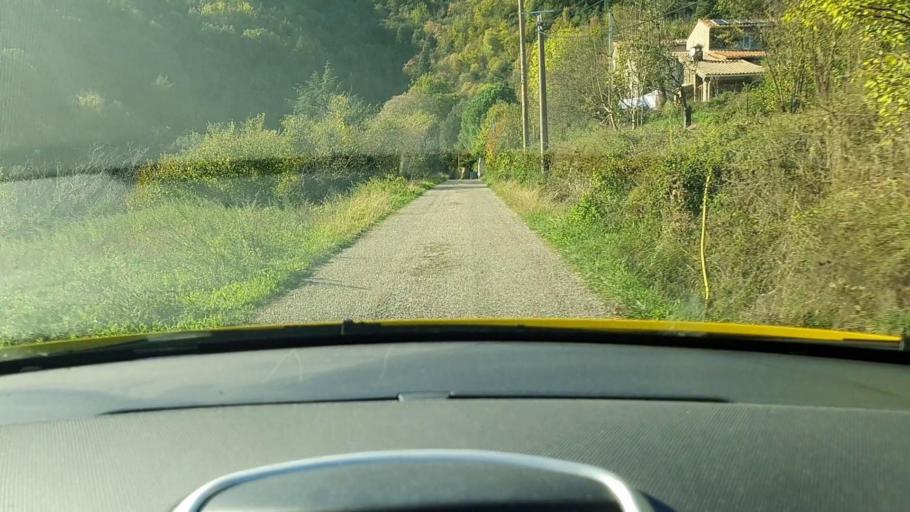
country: FR
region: Languedoc-Roussillon
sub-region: Departement du Gard
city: Sumene
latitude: 43.9801
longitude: 3.6798
